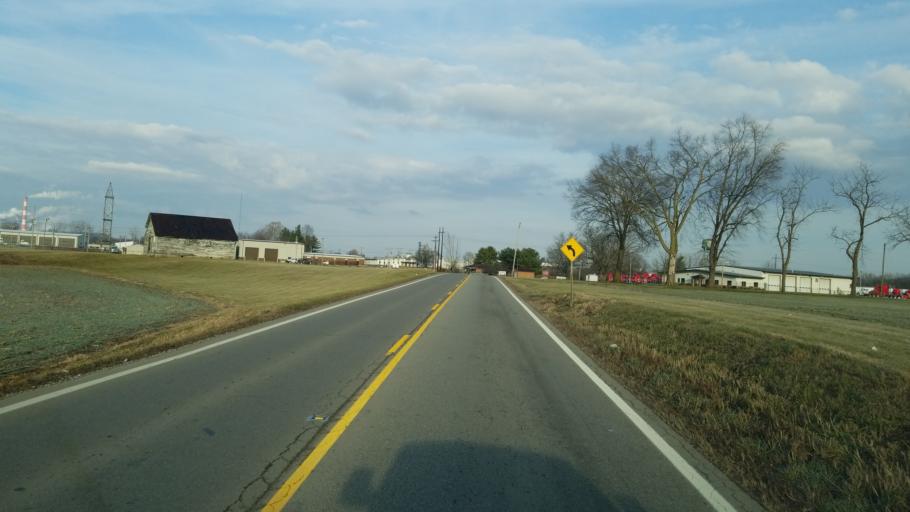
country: US
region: Ohio
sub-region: Ross County
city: Chillicothe
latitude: 39.3179
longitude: -82.9459
